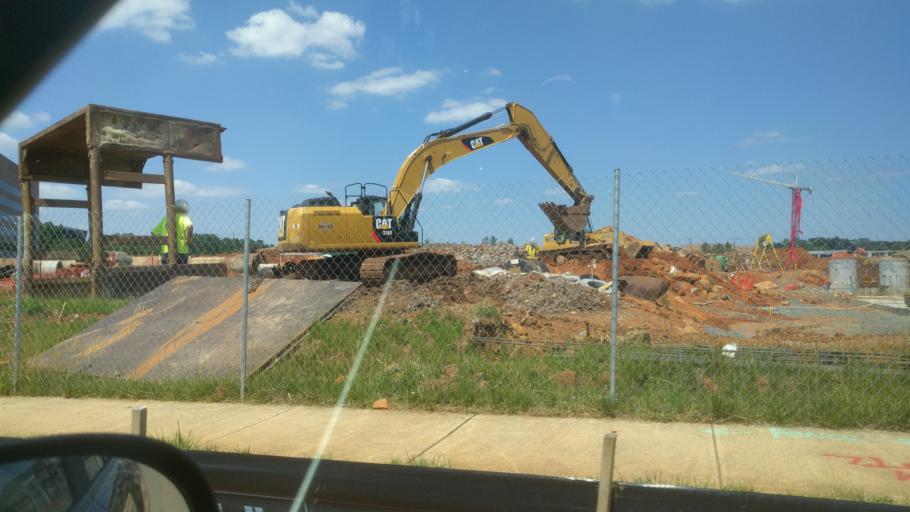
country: US
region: Virginia
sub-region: Fairfax County
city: Floris
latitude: 38.9583
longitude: -77.4203
